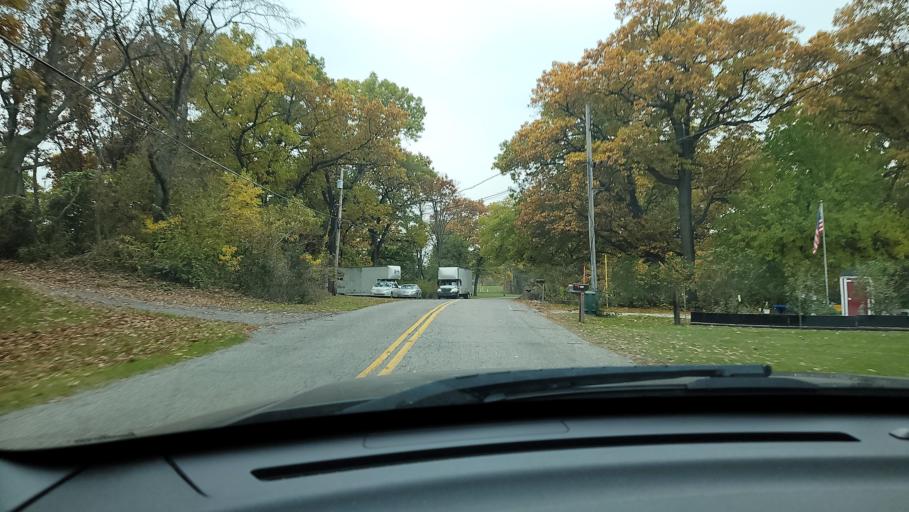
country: US
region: Indiana
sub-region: Porter County
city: Portage
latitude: 41.5875
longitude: -87.2060
